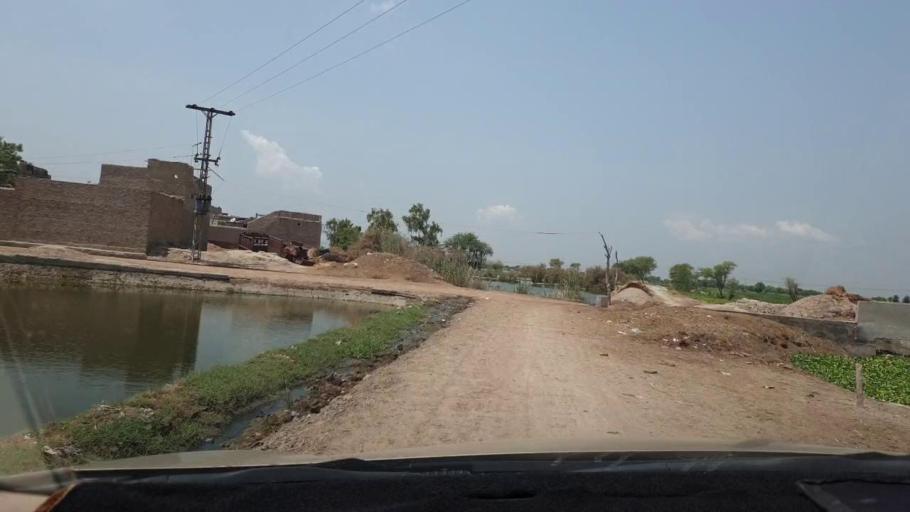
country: PK
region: Sindh
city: Naudero
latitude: 27.6714
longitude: 68.2988
